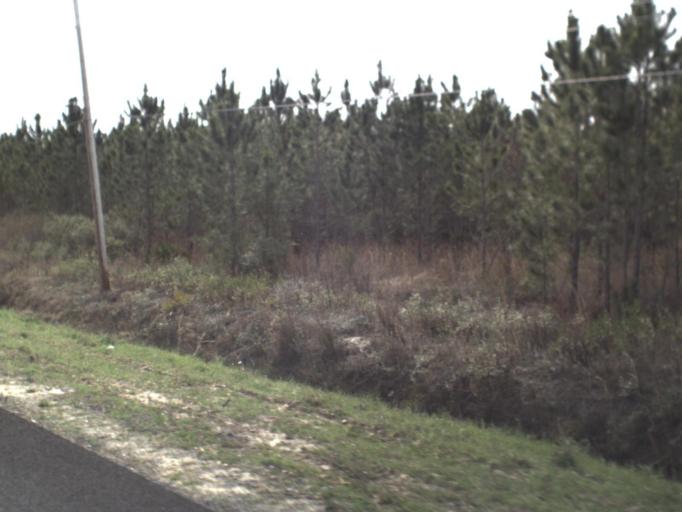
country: US
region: Florida
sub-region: Bay County
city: Youngstown
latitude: 30.4156
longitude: -85.4305
